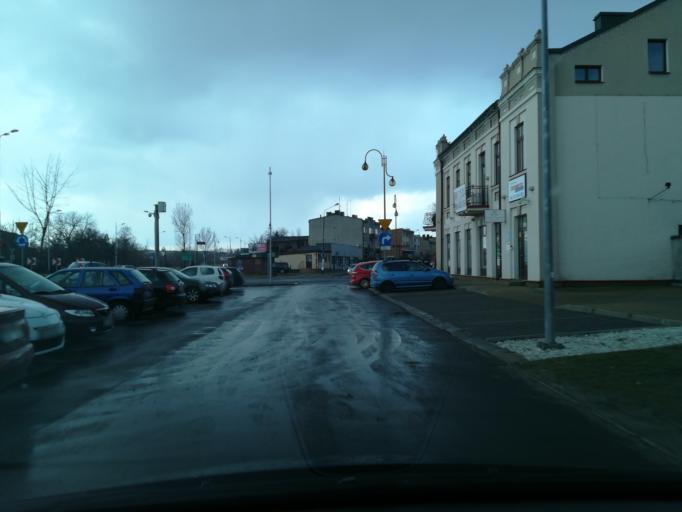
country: PL
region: Lodz Voivodeship
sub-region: Powiat radomszczanski
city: Radomsko
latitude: 51.0653
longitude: 19.4431
